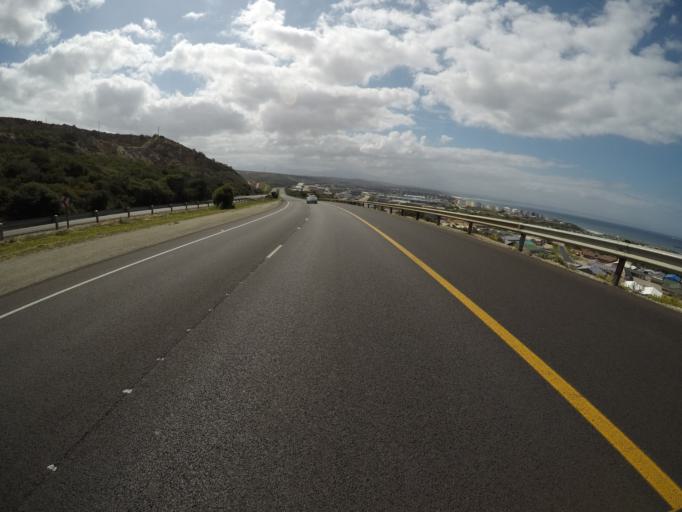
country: ZA
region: Western Cape
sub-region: Eden District Municipality
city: Mossel Bay
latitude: -34.1577
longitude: 22.0997
